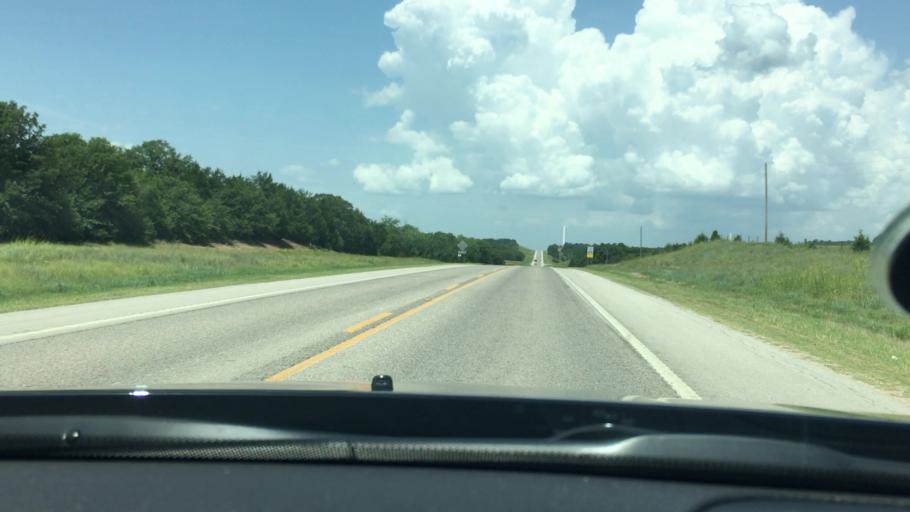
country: US
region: Oklahoma
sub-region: Carter County
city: Dickson
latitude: 34.1003
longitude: -96.9335
